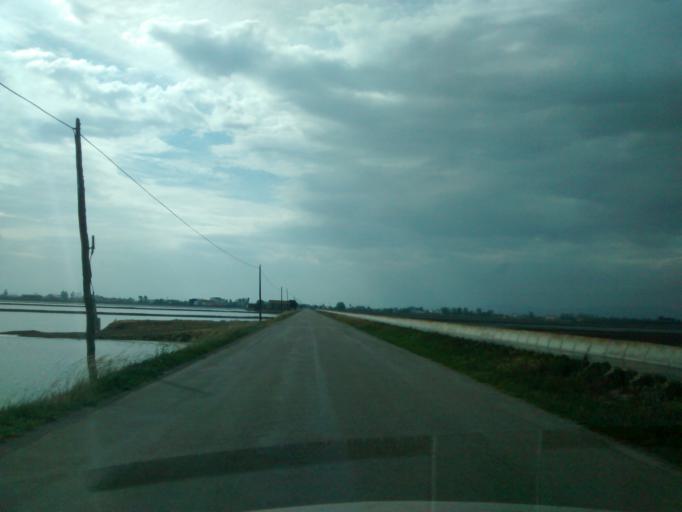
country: ES
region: Catalonia
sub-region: Provincia de Tarragona
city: Deltebre
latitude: 40.6986
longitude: 0.7527
